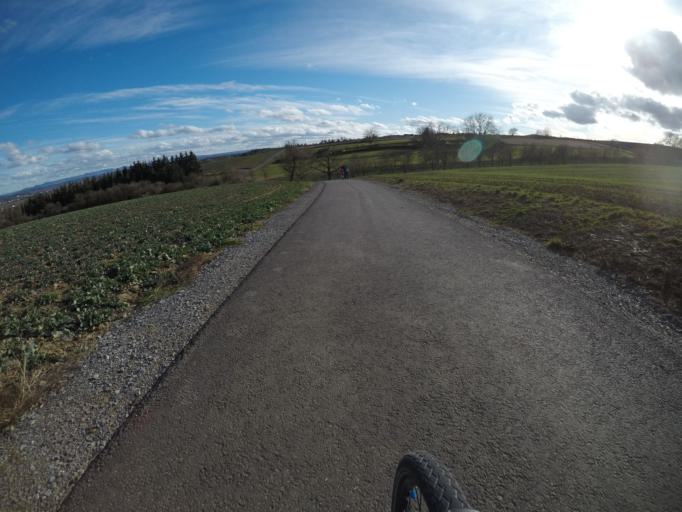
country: DE
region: Baden-Wuerttemberg
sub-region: Regierungsbezirk Stuttgart
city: Herrenberg
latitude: 48.5904
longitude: 8.8448
